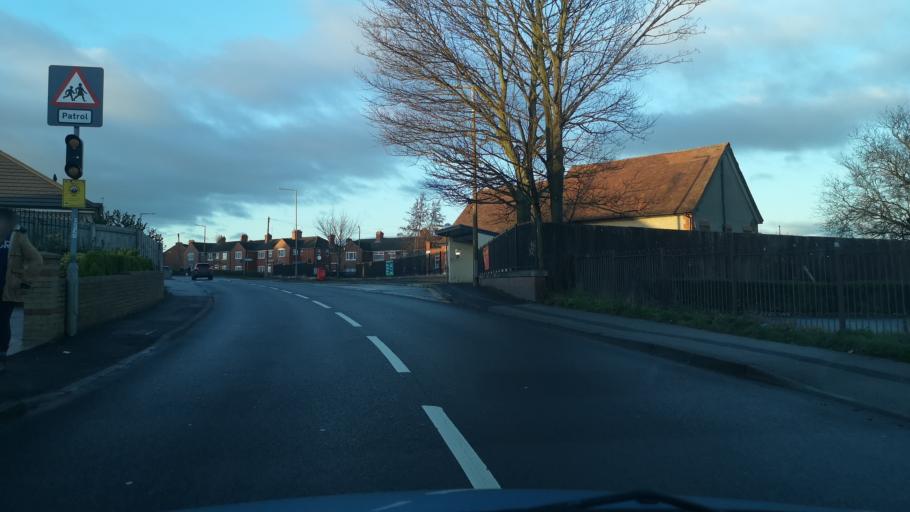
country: GB
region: England
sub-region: Barnsley
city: Great Houghton
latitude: 53.5515
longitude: -1.3469
